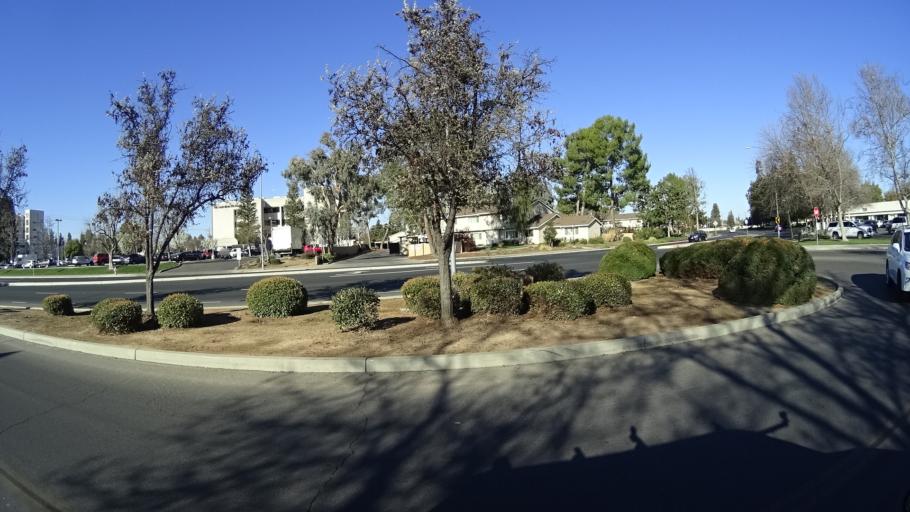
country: US
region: California
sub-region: Fresno County
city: Clovis
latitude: 36.8382
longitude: -119.7629
